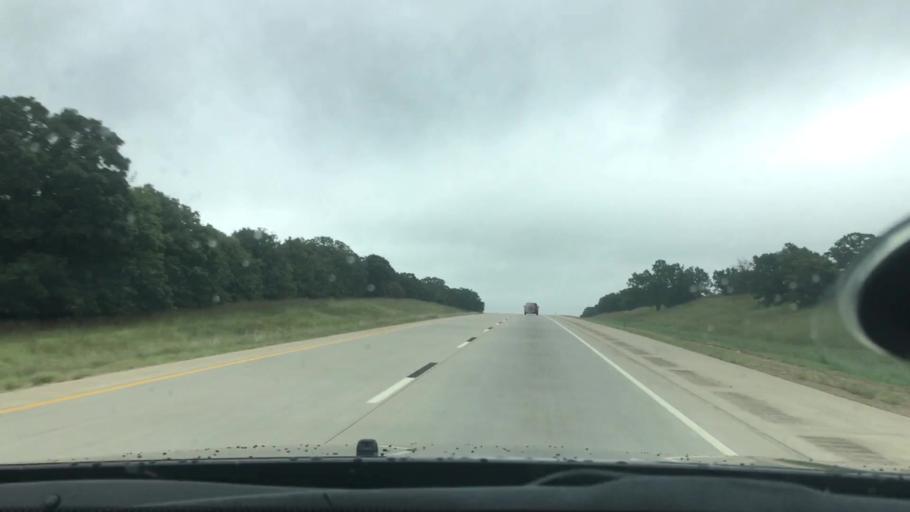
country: US
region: Oklahoma
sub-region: Okfuskee County
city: Boley
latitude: 35.3832
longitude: -96.5129
